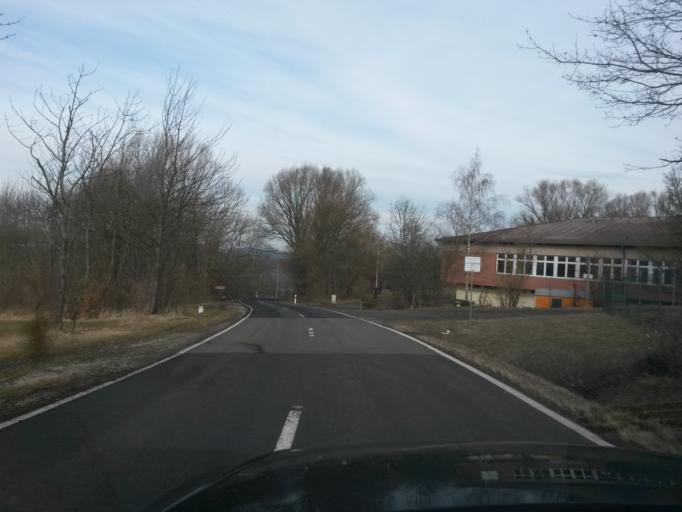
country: DE
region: Hesse
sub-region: Regierungsbezirk Kassel
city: Hilders
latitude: 50.5681
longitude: 10.0146
